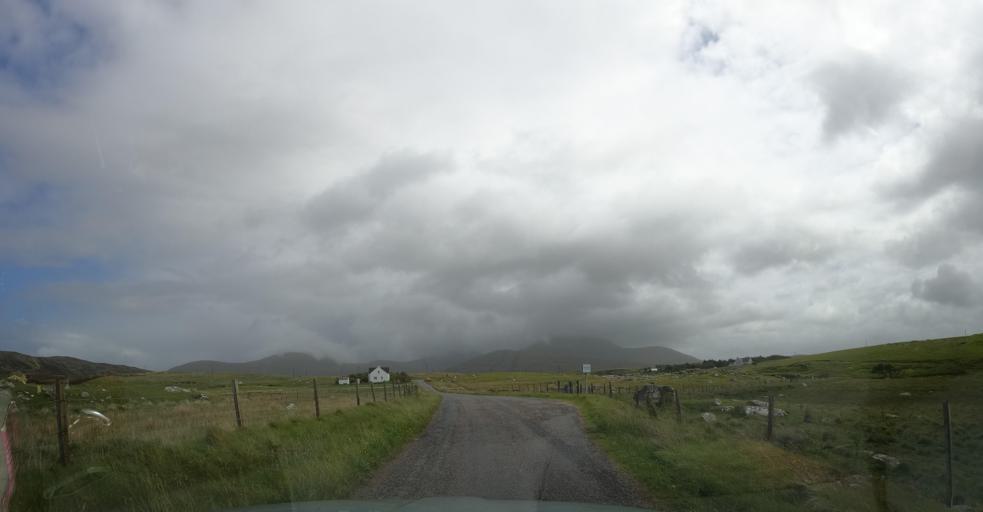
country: GB
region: Scotland
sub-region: Eilean Siar
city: Isle of South Uist
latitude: 57.2903
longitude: -7.3708
